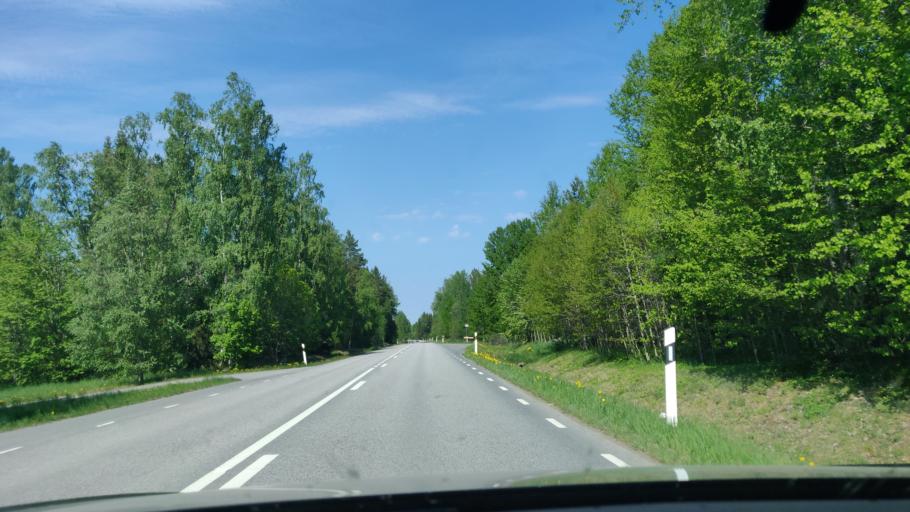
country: SE
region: Uppsala
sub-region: Heby Kommun
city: OEstervala
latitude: 60.1514
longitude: 17.2006
